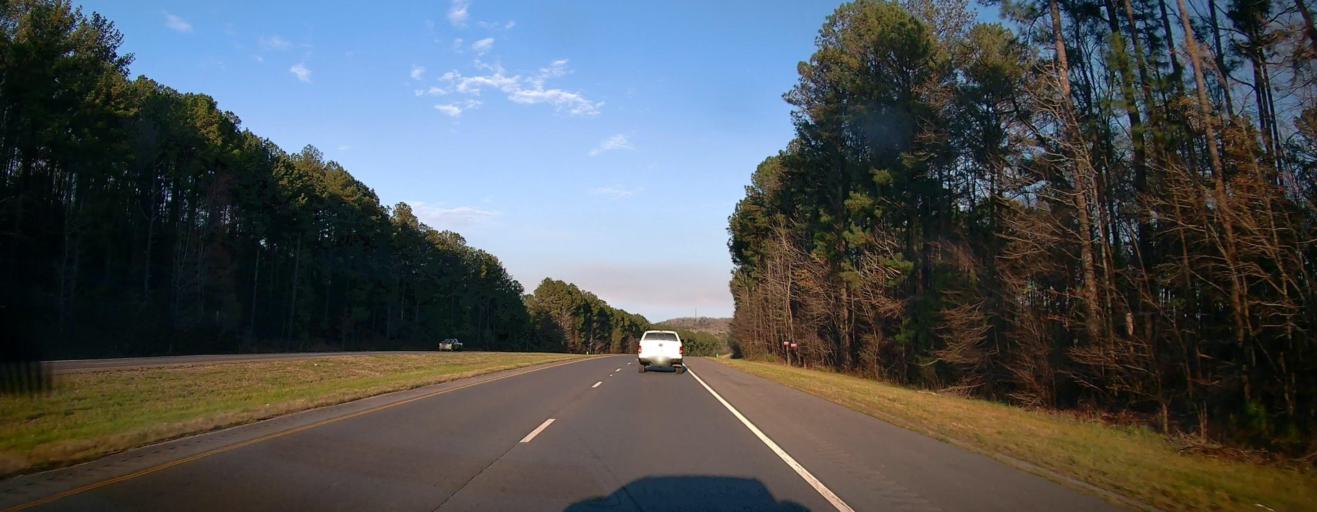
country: US
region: Alabama
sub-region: Shelby County
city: Westover
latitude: 33.3573
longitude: -86.5094
